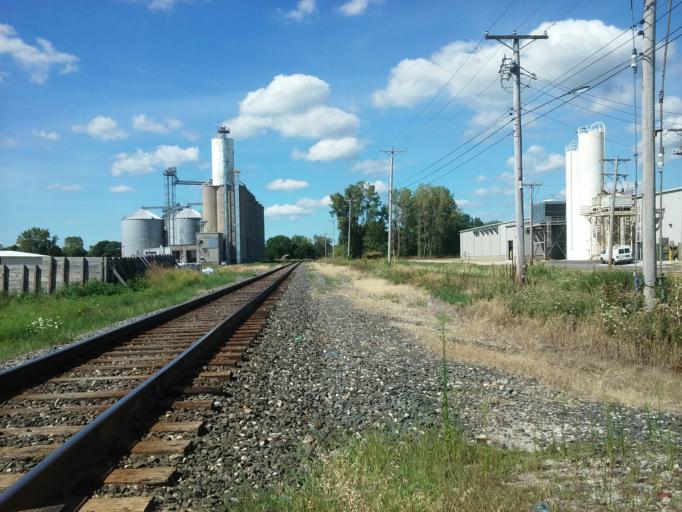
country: US
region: Ohio
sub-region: Wood County
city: Bowling Green
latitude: 41.3567
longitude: -83.6458
